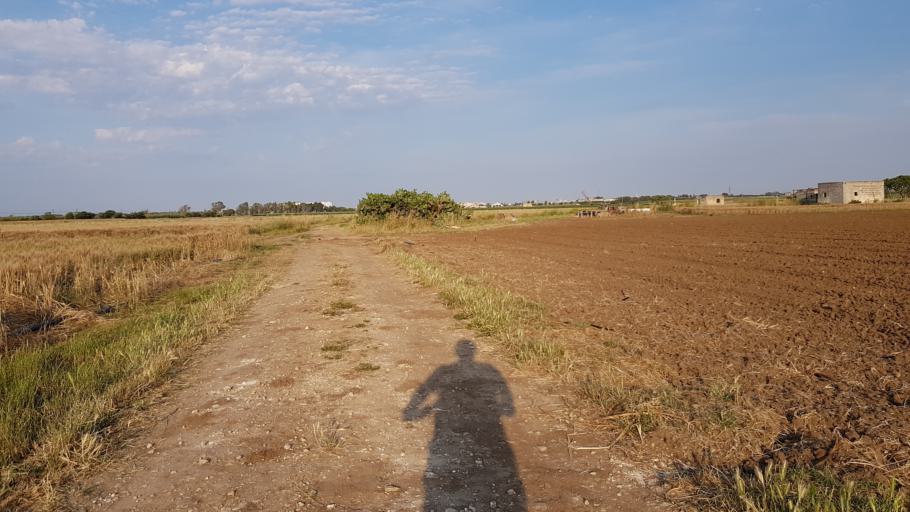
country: IT
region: Apulia
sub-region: Provincia di Brindisi
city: Brindisi
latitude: 40.6249
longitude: 17.8837
